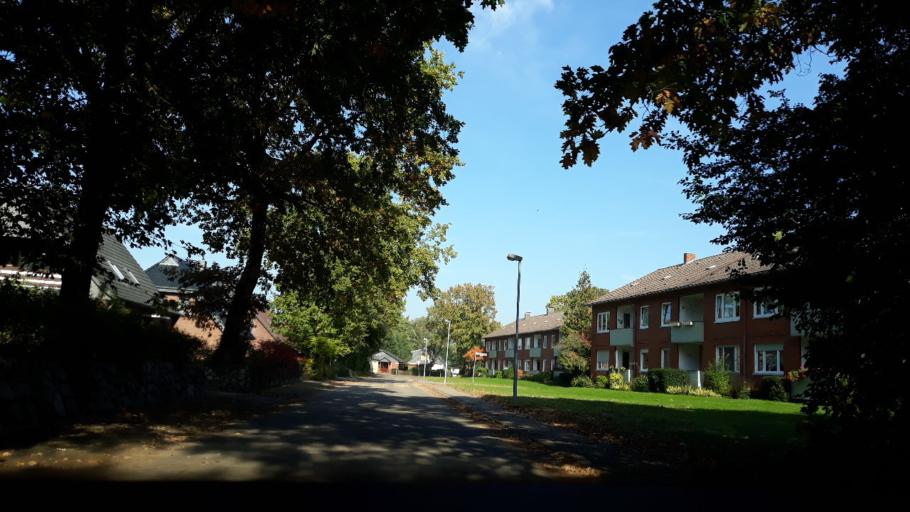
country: DE
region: Schleswig-Holstein
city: Kropp
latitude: 54.4143
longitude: 9.5177
